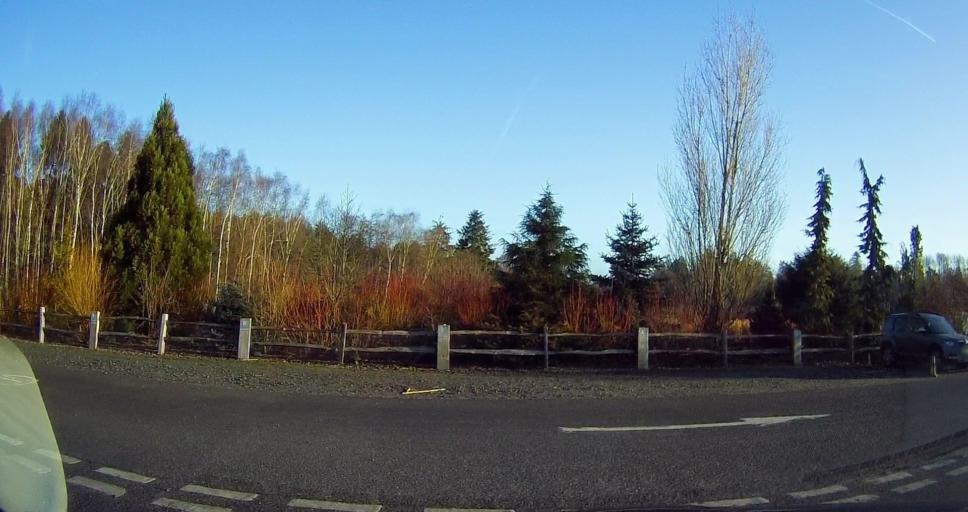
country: GB
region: England
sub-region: Kent
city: Hawkhurst
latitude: 51.0726
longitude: 0.4471
